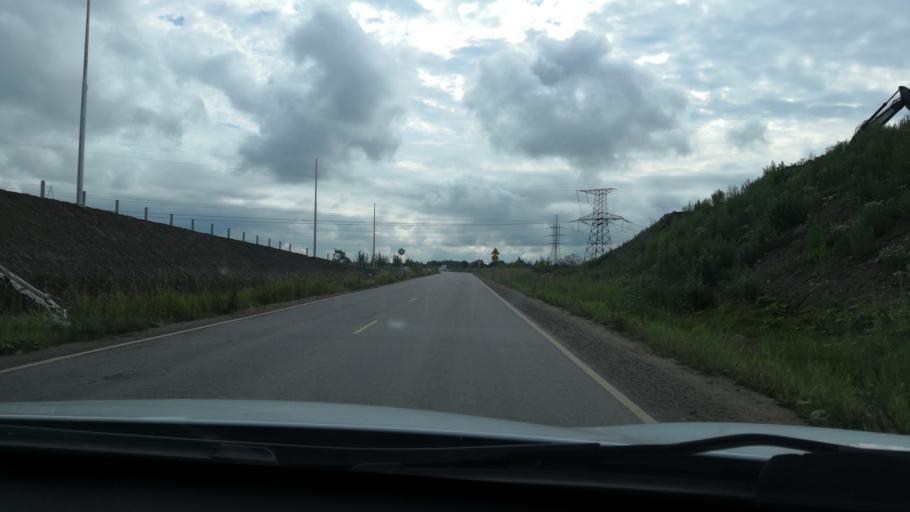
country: RU
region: Leningrad
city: Fedorovskoye
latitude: 59.7063
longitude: 30.5459
